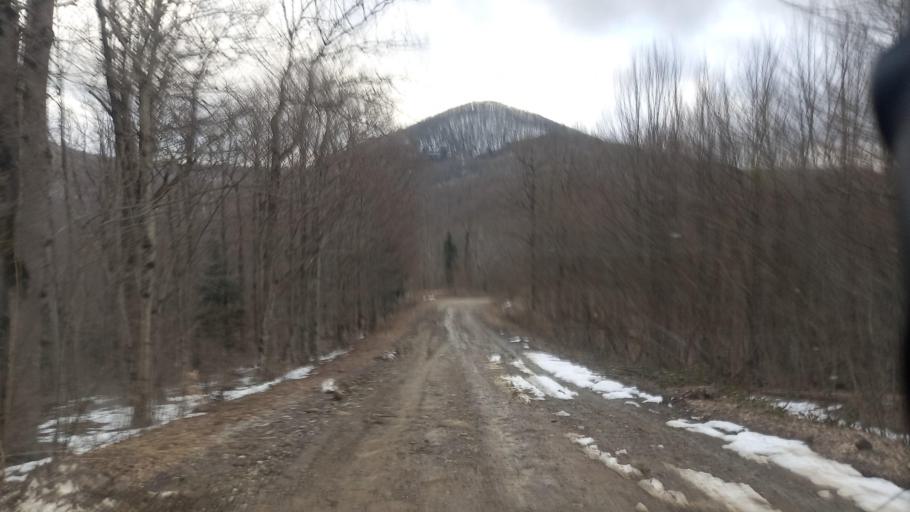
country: RU
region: Krasnodarskiy
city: Dzhubga
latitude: 44.5079
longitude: 38.7770
